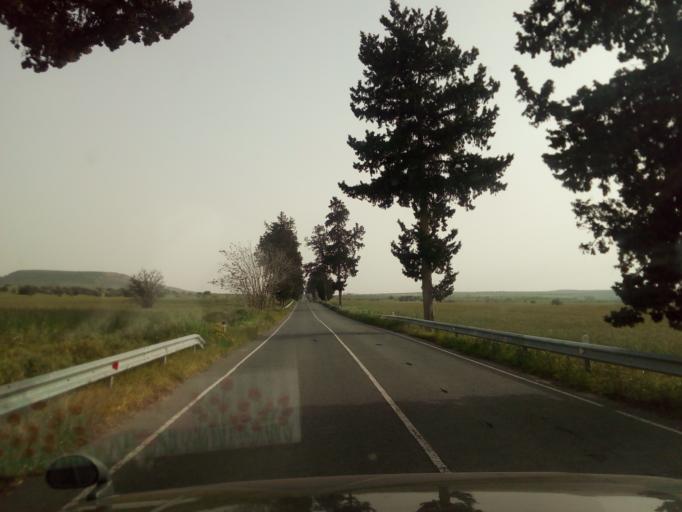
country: CY
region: Lefkosia
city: Lympia
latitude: 35.0291
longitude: 33.4928
